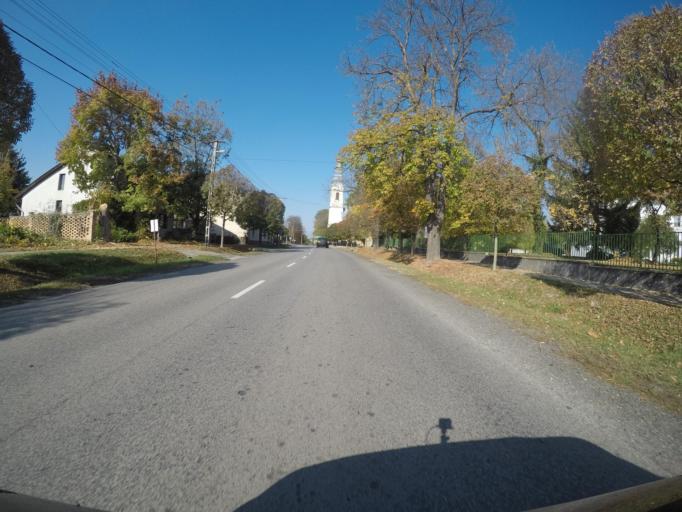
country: HU
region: Tolna
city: Nagydorog
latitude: 46.6280
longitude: 18.6562
